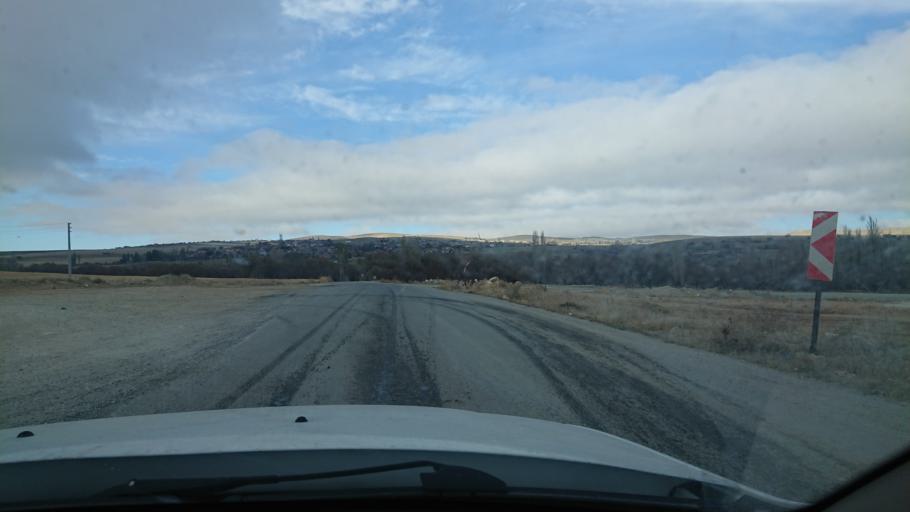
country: TR
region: Aksaray
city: Ortakoy
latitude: 38.7521
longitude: 34.0226
